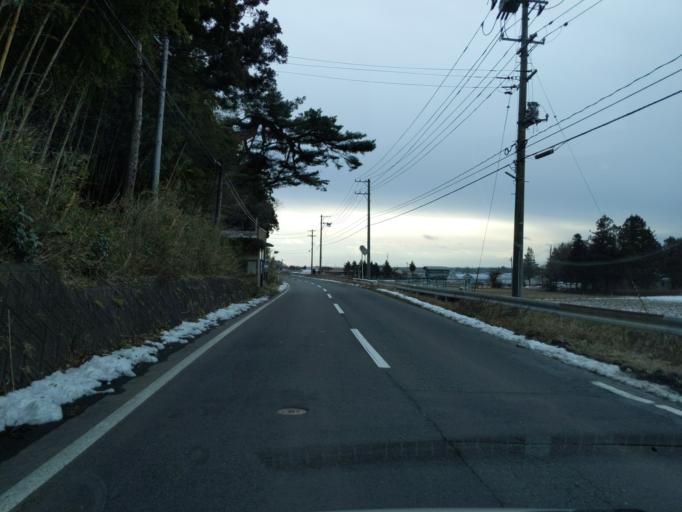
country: JP
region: Iwate
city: Mizusawa
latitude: 39.1664
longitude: 141.1951
